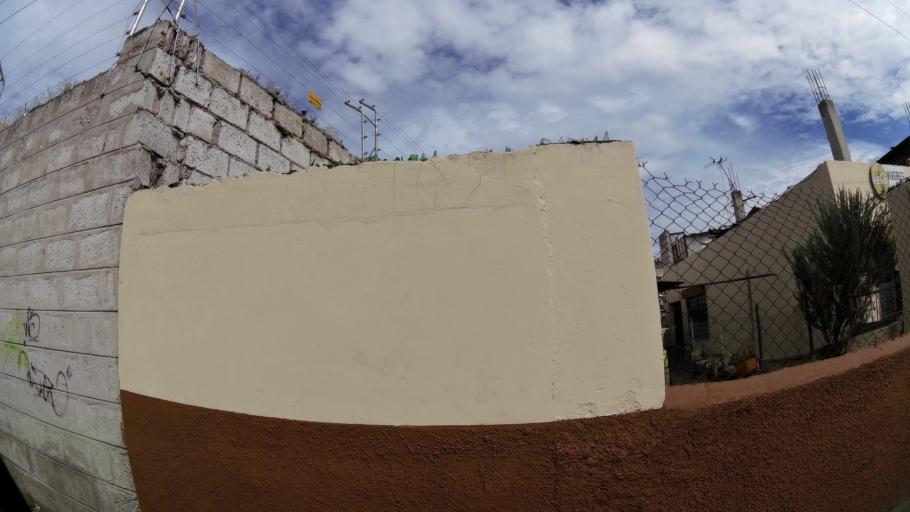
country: EC
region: Tungurahua
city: Ambato
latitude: -1.2493
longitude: -78.6181
